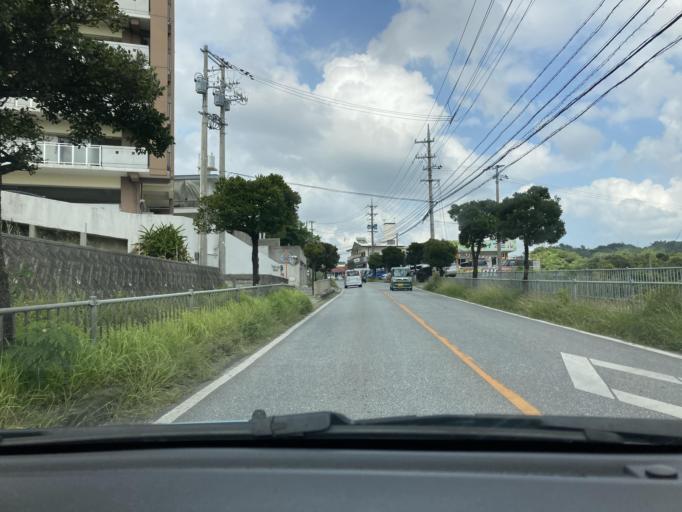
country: JP
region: Okinawa
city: Chatan
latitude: 26.2853
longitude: 127.7858
